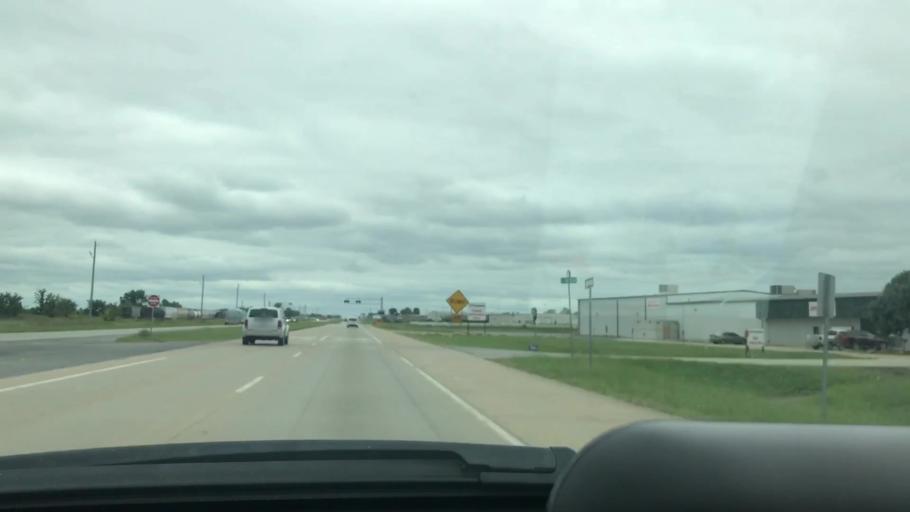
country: US
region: Oklahoma
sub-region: Mayes County
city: Chouteau
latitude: 36.2350
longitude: -95.3386
